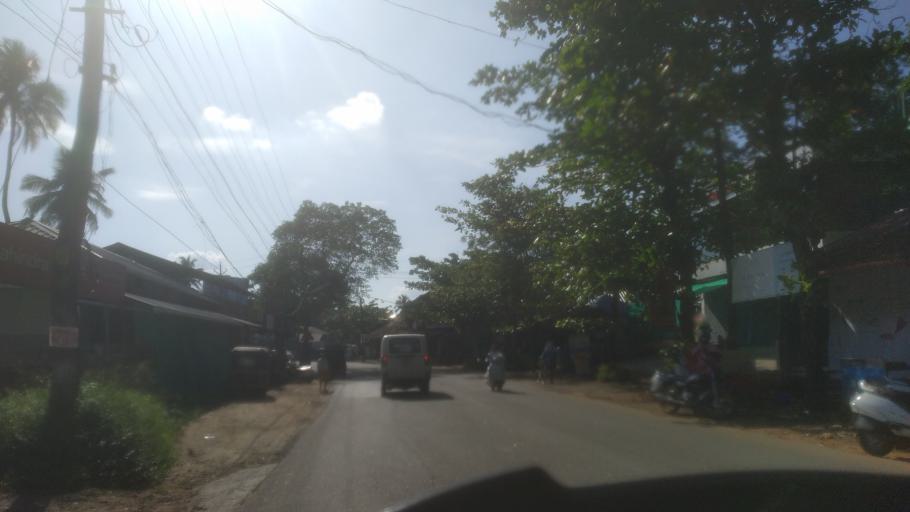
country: IN
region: Kerala
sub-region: Ernakulam
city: Muvattupuzha
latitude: 9.9796
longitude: 76.5515
